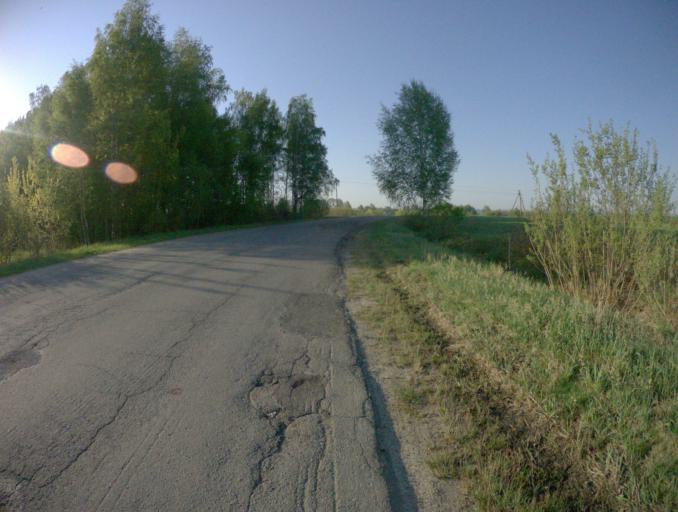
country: RU
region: Vladimir
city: Vyazniki
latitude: 56.2738
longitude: 42.1719
